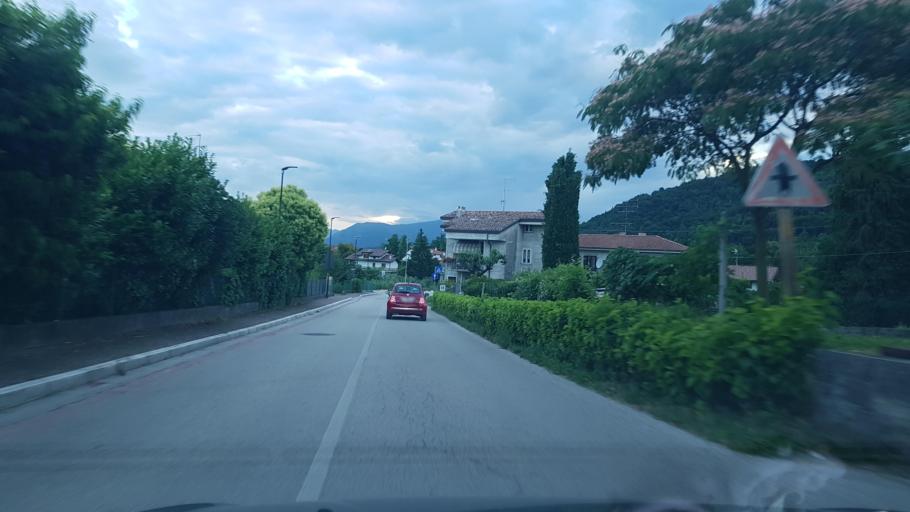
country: IT
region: Friuli Venezia Giulia
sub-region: Provincia di Udine
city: San Giacomo
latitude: 46.1803
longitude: 12.9759
